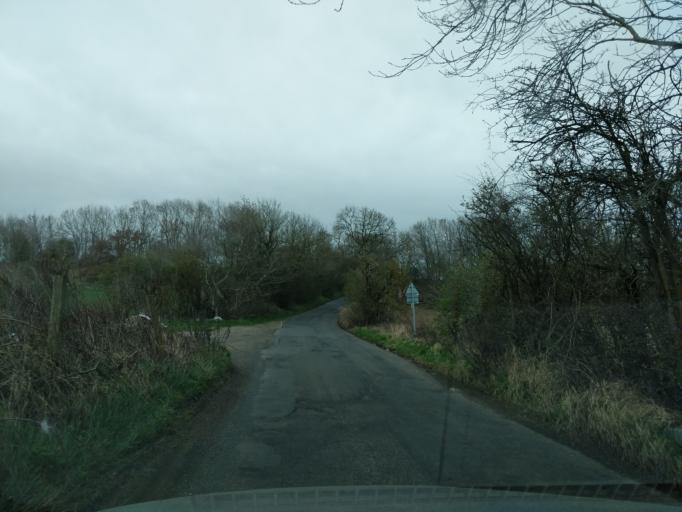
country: GB
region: Scotland
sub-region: Edinburgh
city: Balerno
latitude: 55.8938
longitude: -3.3480
